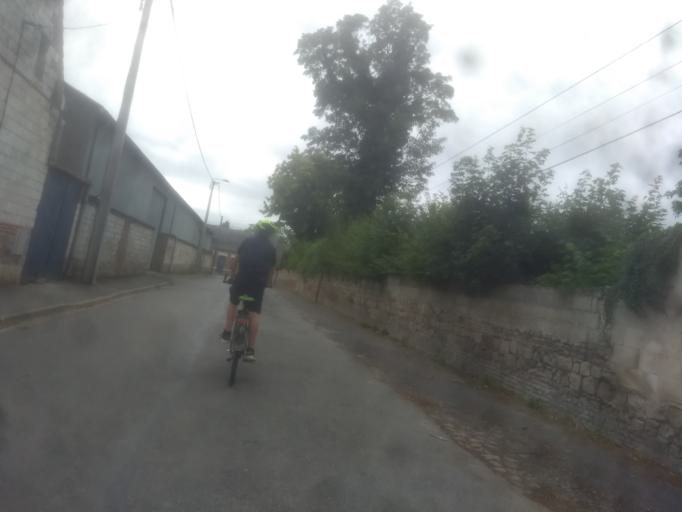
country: FR
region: Nord-Pas-de-Calais
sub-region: Departement du Pas-de-Calais
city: Maroeuil
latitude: 50.3255
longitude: 2.7014
